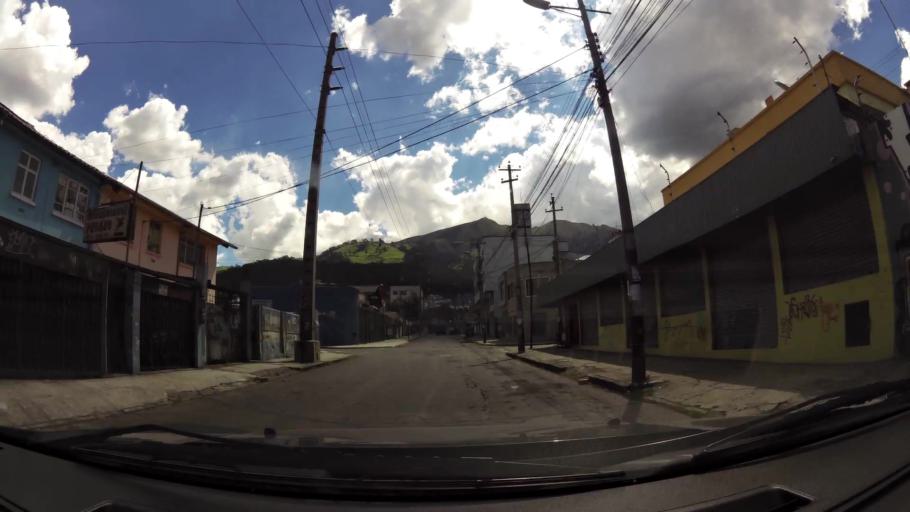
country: EC
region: Pichincha
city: Quito
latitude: -0.2036
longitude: -78.5028
